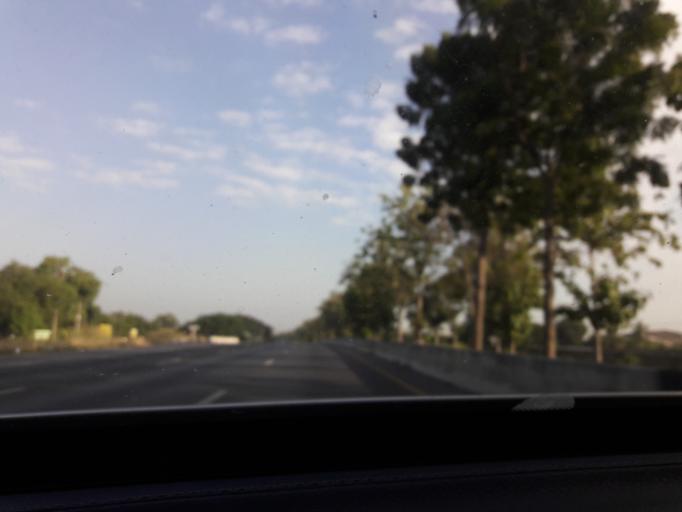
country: TH
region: Ang Thong
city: Chaiyo
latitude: 14.6439
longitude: 100.4747
